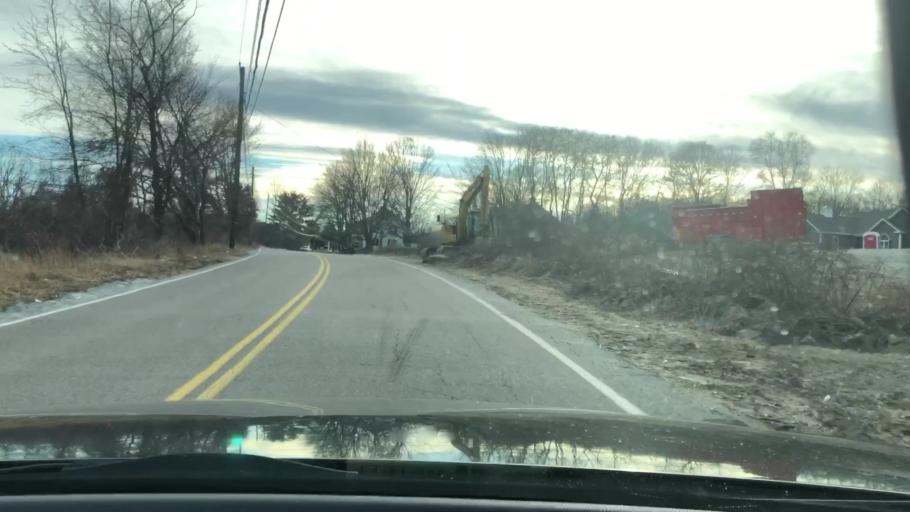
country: US
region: Massachusetts
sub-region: Worcester County
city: Blackstone
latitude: 42.0561
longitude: -71.5302
